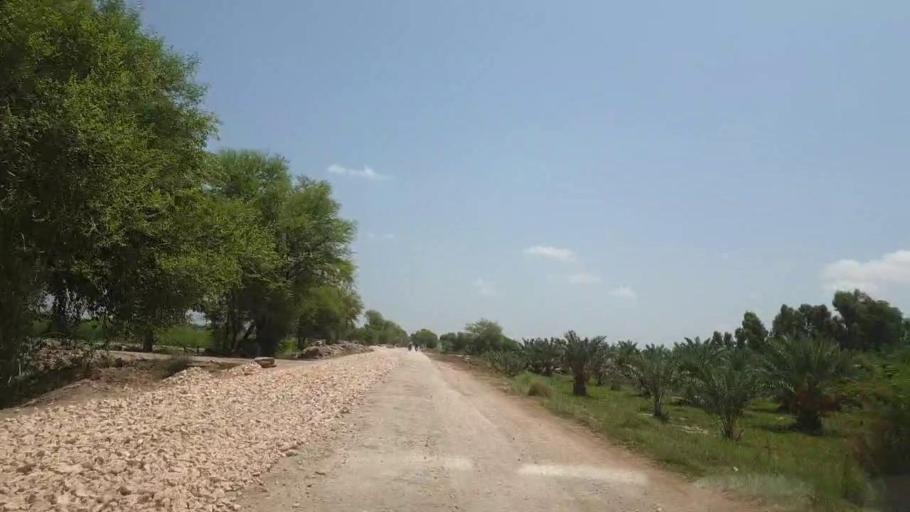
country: PK
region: Sindh
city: Pano Aqil
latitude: 27.6660
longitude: 69.1846
